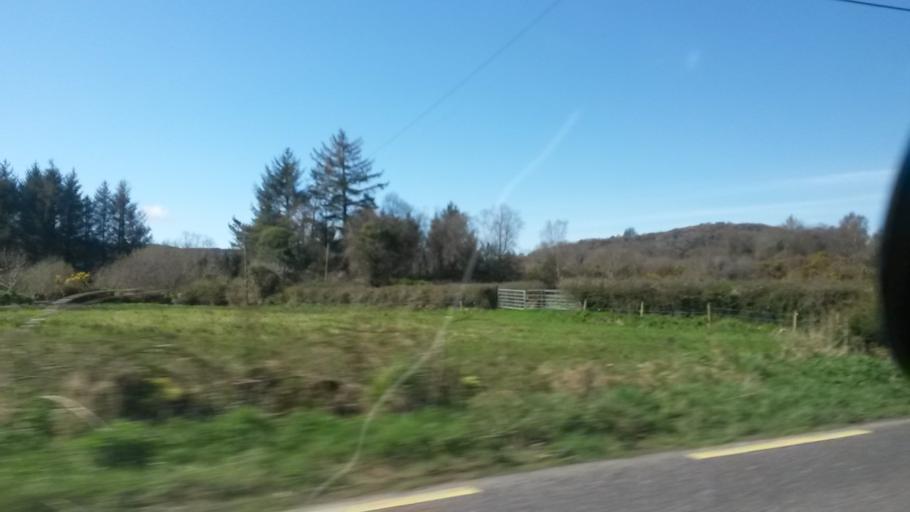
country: IE
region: Munster
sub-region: County Cork
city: Millstreet
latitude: 51.9335
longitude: -9.1306
